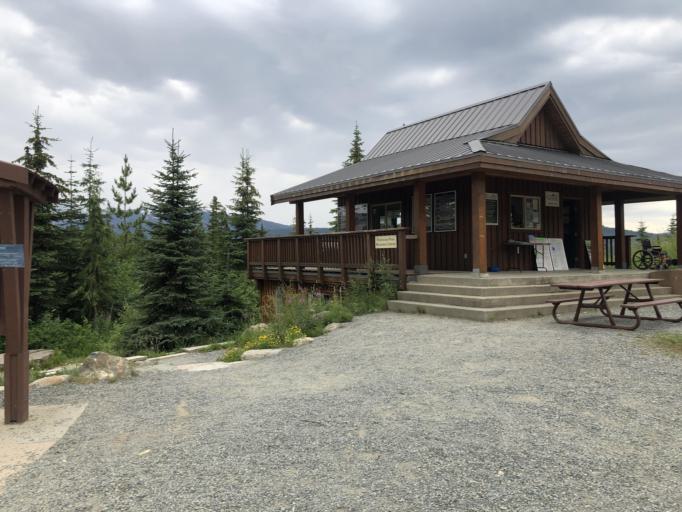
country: CA
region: British Columbia
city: Campbell River
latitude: 49.7452
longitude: -125.3193
